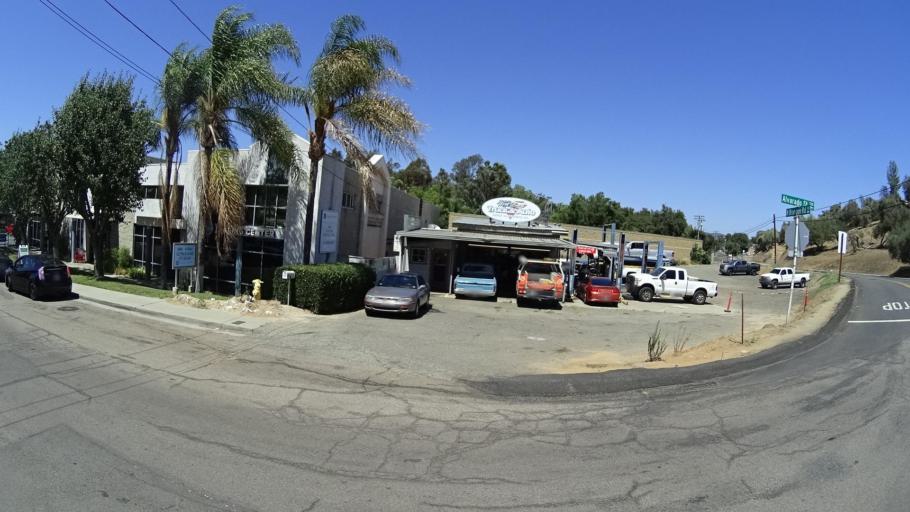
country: US
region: California
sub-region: San Diego County
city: Fallbrook
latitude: 33.3819
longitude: -117.2449
